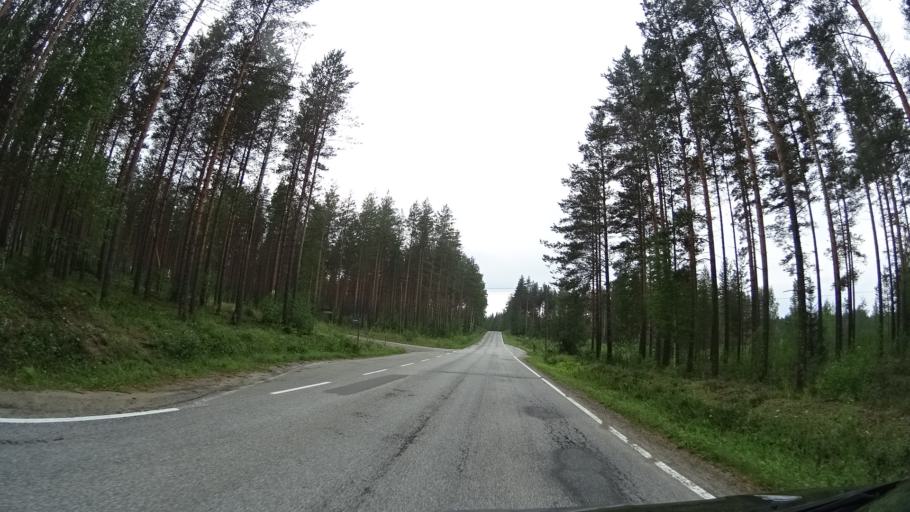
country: FI
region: Southern Savonia
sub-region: Savonlinna
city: Punkaharju
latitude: 61.7477
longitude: 29.4951
